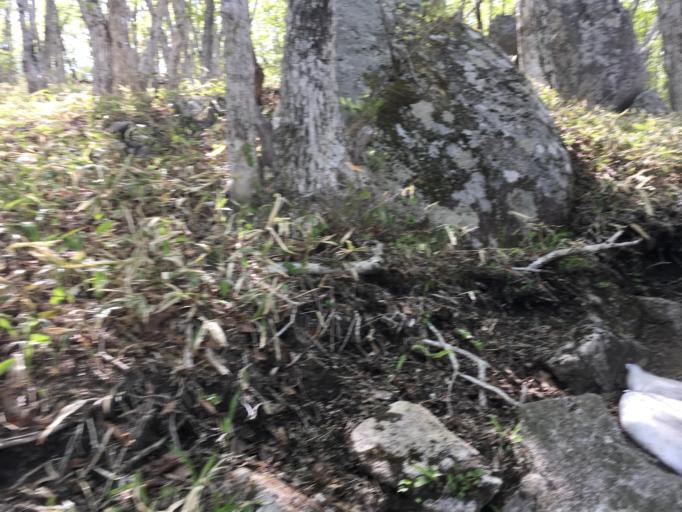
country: JP
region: Iwate
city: Ofunato
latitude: 39.1893
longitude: 141.7310
